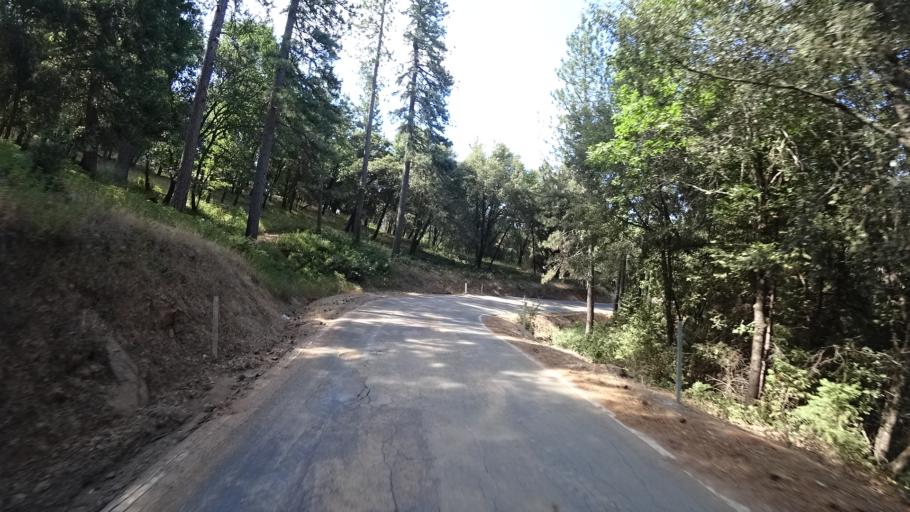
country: US
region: California
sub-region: Amador County
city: Pioneer
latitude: 38.3701
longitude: -120.5080
